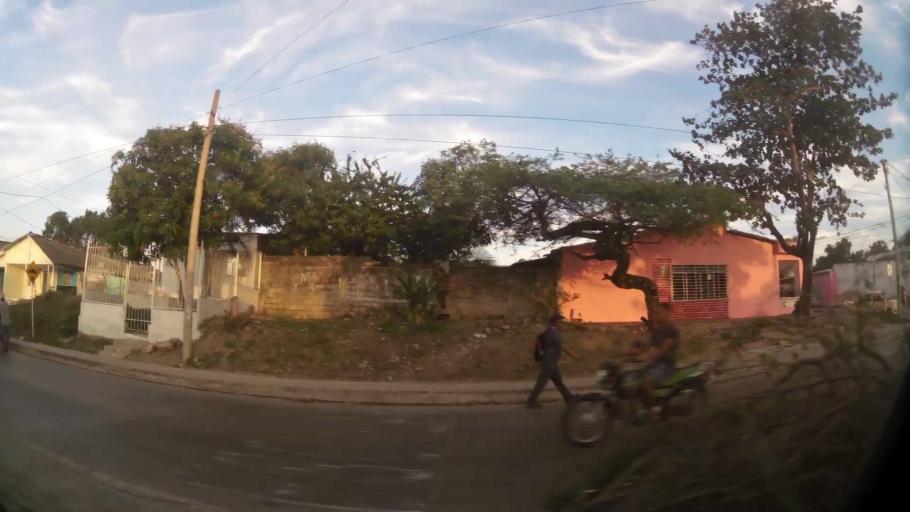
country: CO
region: Atlantico
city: Barranquilla
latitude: 10.9507
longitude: -74.8217
